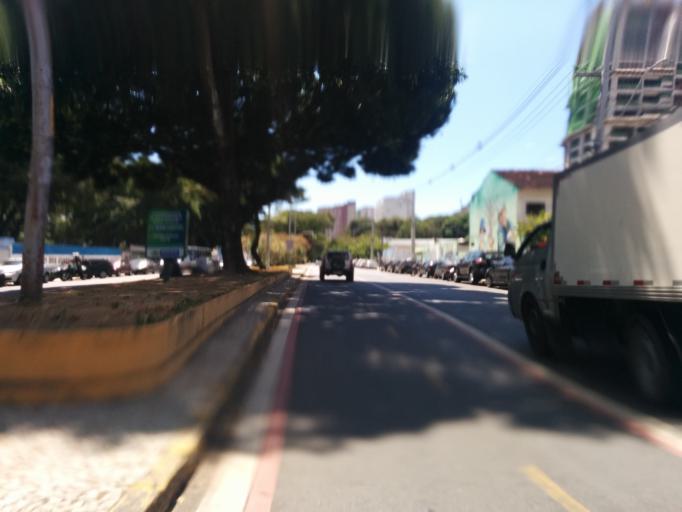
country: BR
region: Pernambuco
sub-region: Recife
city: Recife
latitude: -8.0509
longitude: -34.8861
